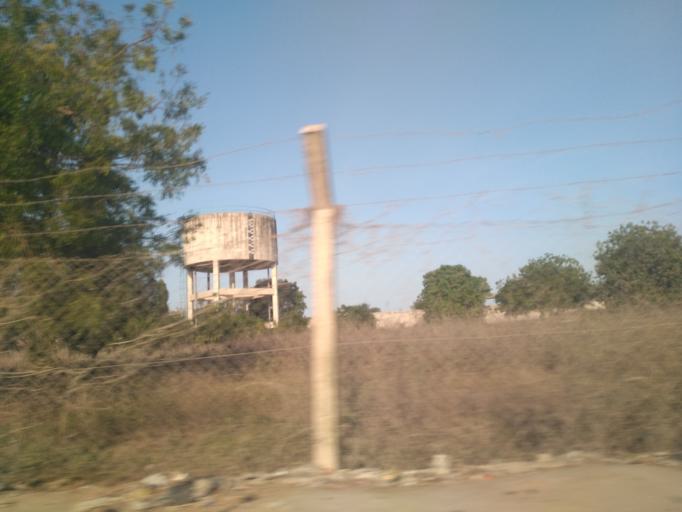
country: TZ
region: Pwani
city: Vikindu
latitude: -6.9210
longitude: 39.2678
